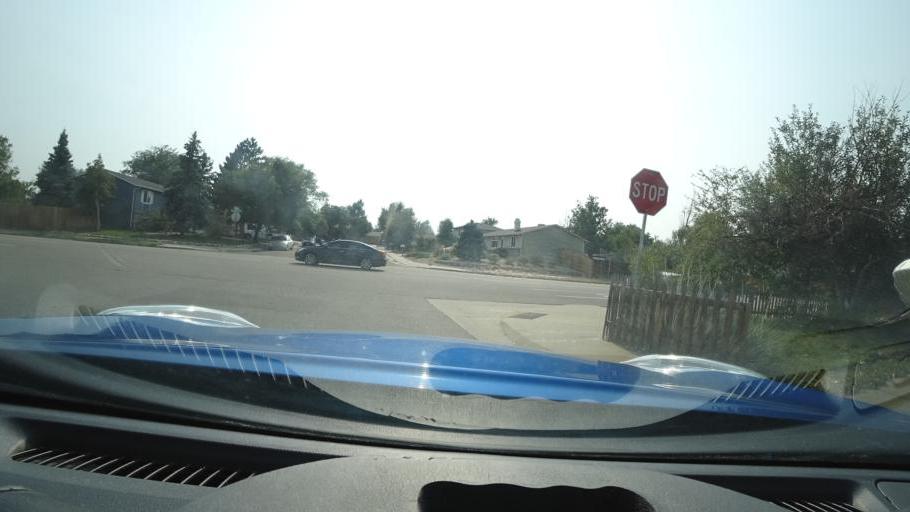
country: US
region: Colorado
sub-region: Adams County
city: Aurora
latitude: 39.6650
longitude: -104.8019
